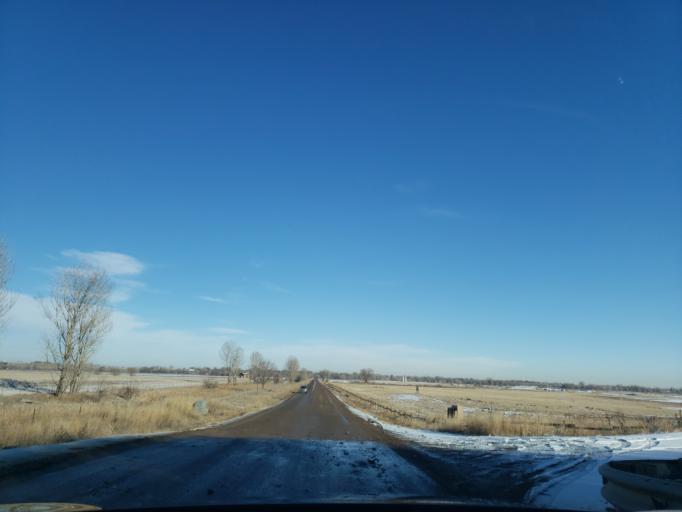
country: US
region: Colorado
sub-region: Larimer County
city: Fort Collins
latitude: 40.5378
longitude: -105.0165
